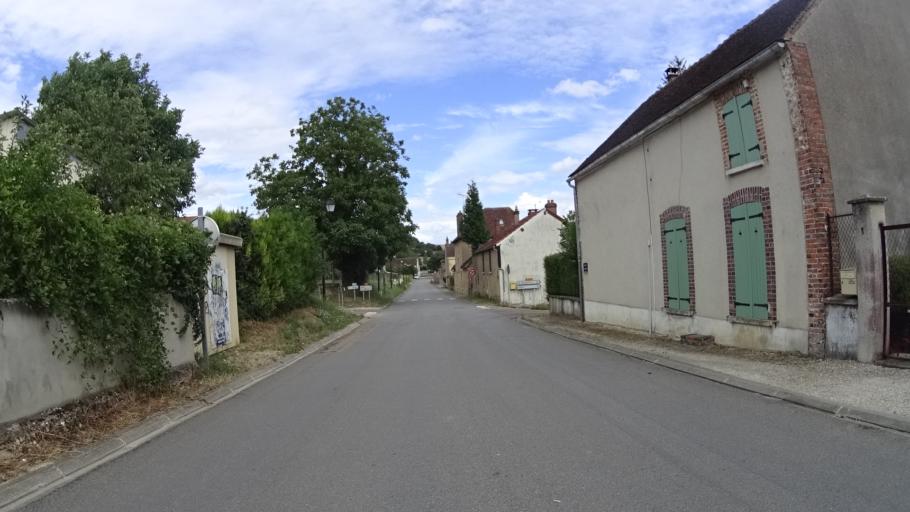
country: FR
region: Bourgogne
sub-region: Departement de l'Yonne
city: Saint-Julien-du-Sault
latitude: 47.9875
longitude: 3.2884
